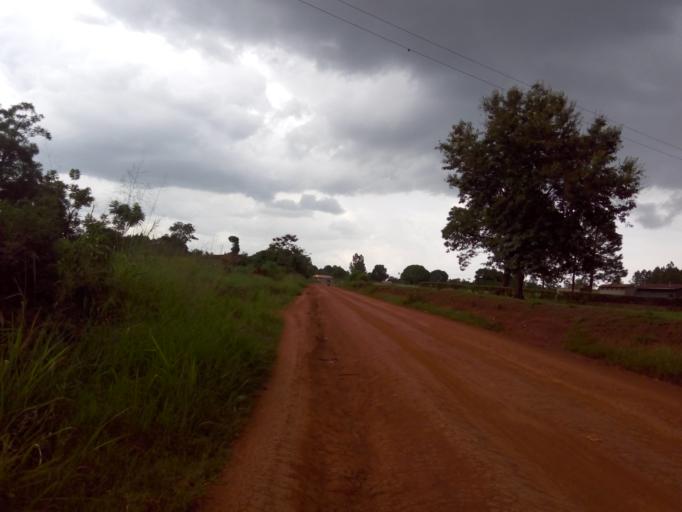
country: UG
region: Western Region
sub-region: Masindi District
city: Masindi
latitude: 1.6832
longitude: 31.7068
